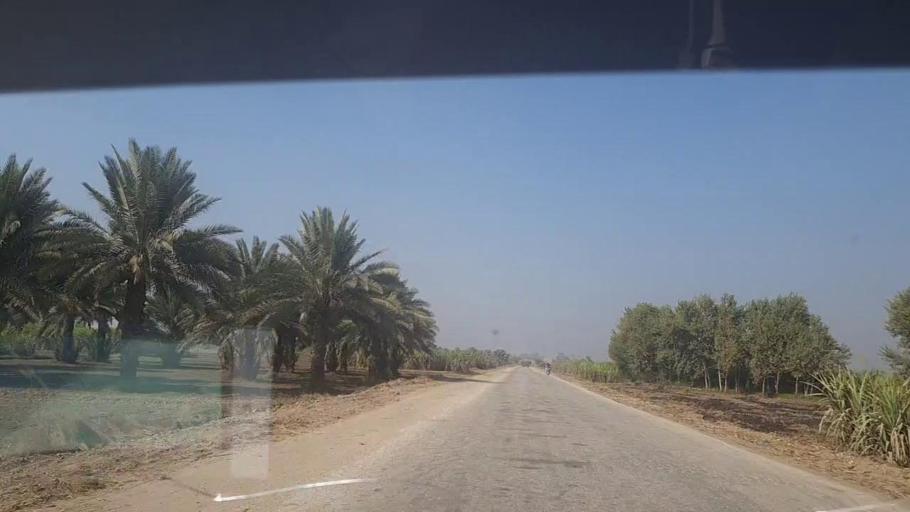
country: PK
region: Sindh
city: Kot Diji
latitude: 27.4219
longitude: 68.6597
